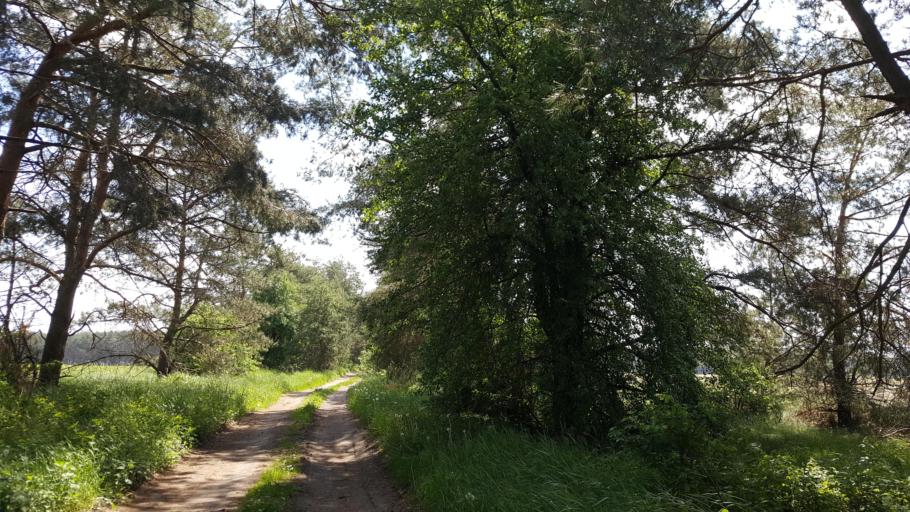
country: BY
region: Brest
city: Kamyanyets
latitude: 52.3967
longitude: 23.8592
